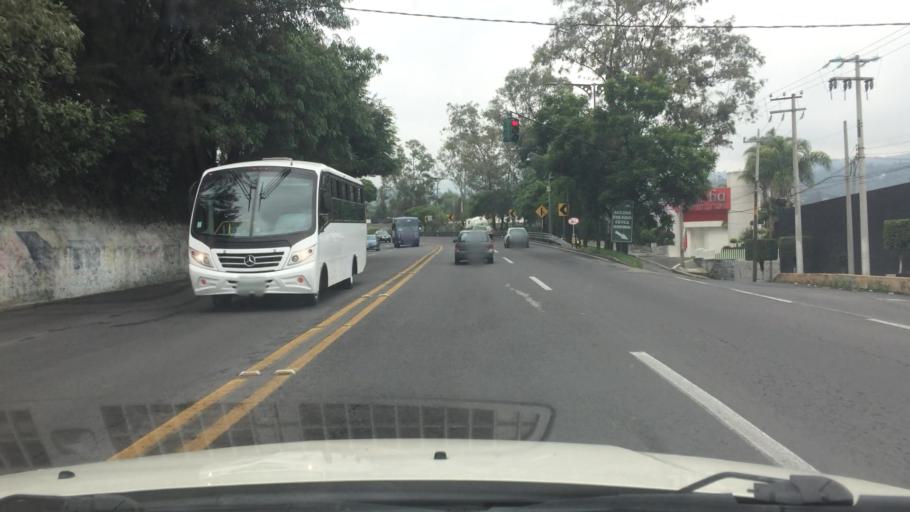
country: MX
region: Mexico City
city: Tlalpan
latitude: 19.2626
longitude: -99.1739
